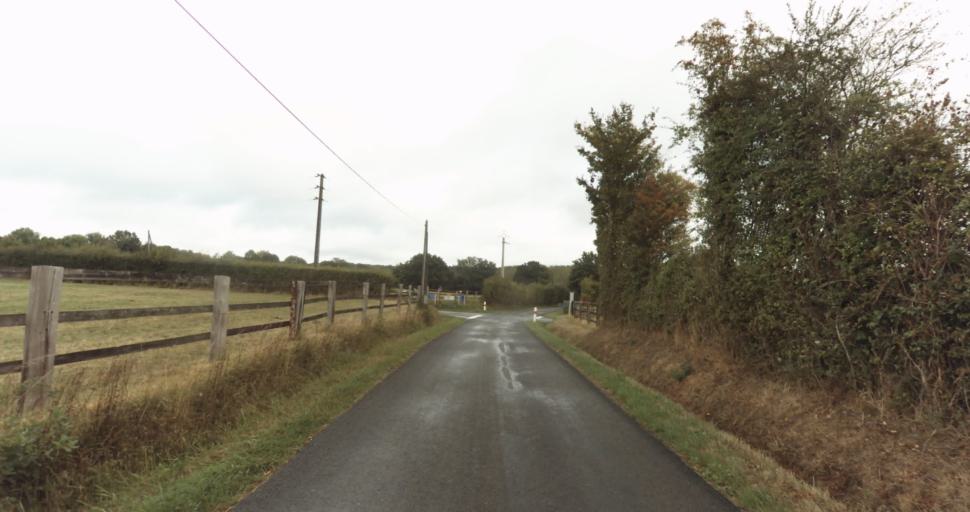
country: FR
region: Lower Normandy
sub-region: Departement de l'Orne
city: Sainte-Gauburge-Sainte-Colombe
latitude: 48.7445
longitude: 0.4714
